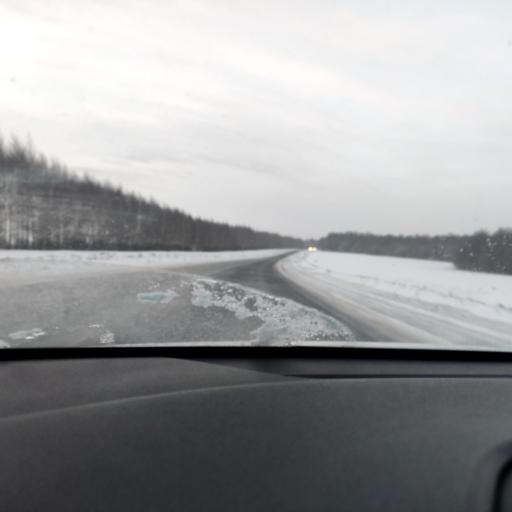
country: RU
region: Tatarstan
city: Verkhniy Uslon
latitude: 55.6584
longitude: 48.8560
